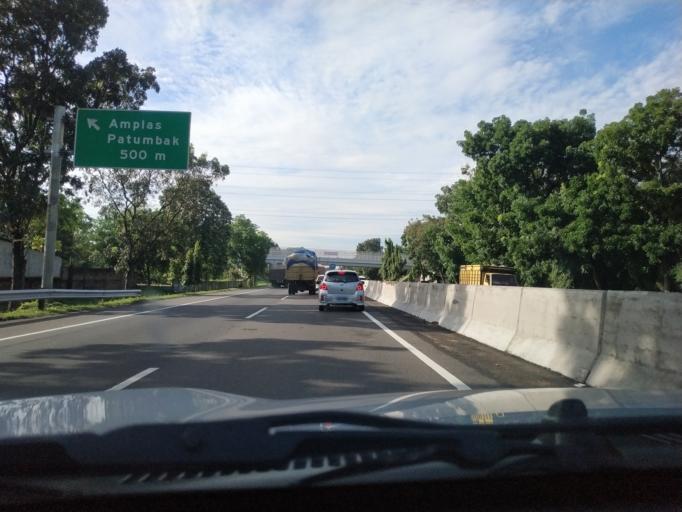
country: ID
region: North Sumatra
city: Deli Tua
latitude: 3.5528
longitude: 98.7252
